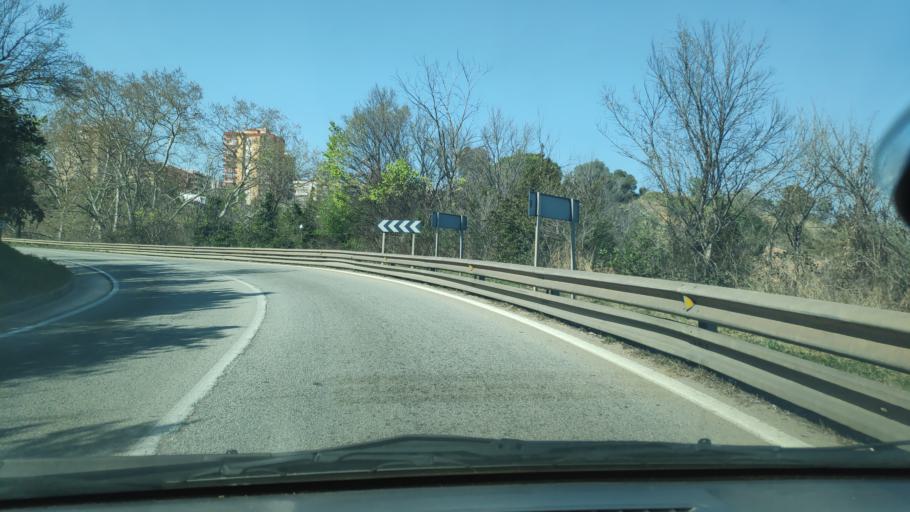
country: ES
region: Catalonia
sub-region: Provincia de Barcelona
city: Sabadell
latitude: 41.5329
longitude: 2.1227
